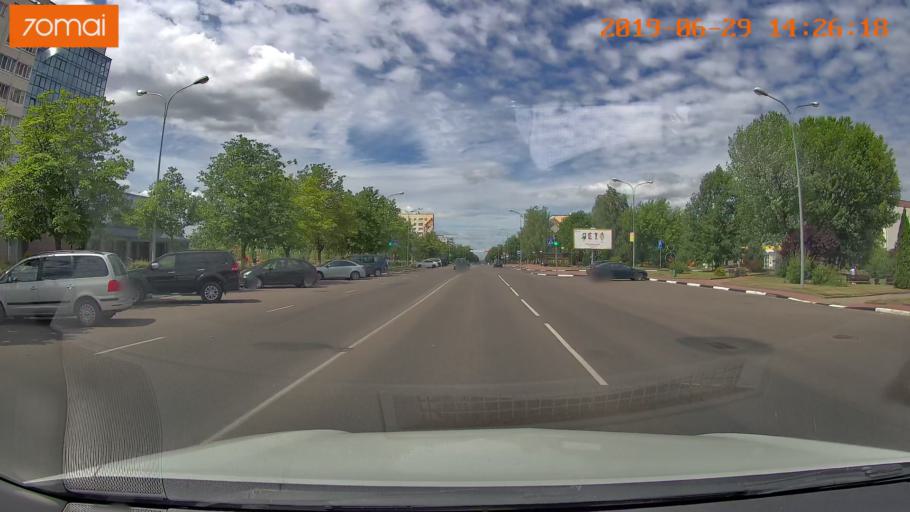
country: BY
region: Minsk
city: Salihorsk
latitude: 52.7818
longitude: 27.5426
